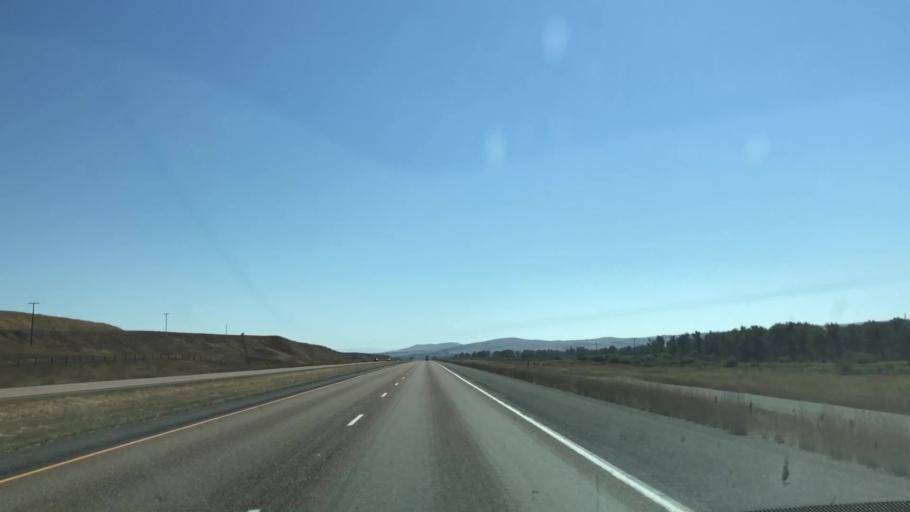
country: US
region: Montana
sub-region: Granite County
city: Philipsburg
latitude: 46.6251
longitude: -113.0778
